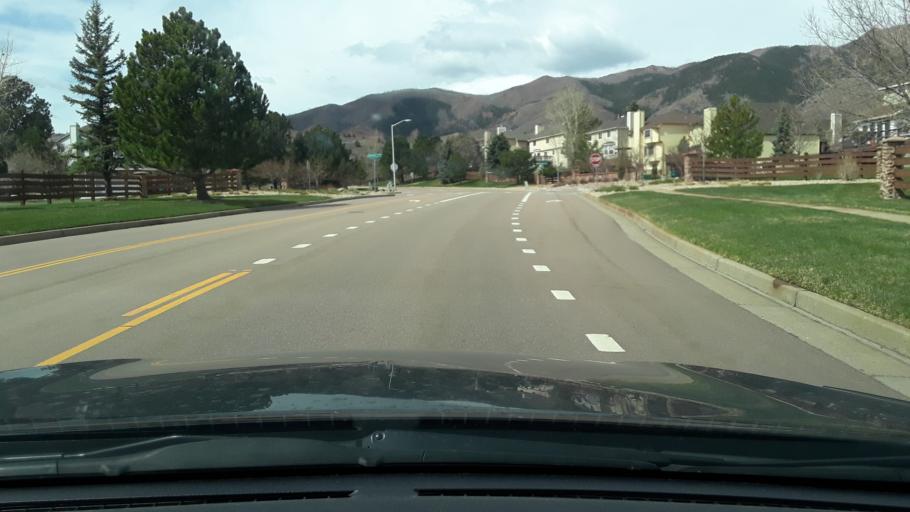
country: US
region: Colorado
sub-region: El Paso County
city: Air Force Academy
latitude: 38.9492
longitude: -104.8669
